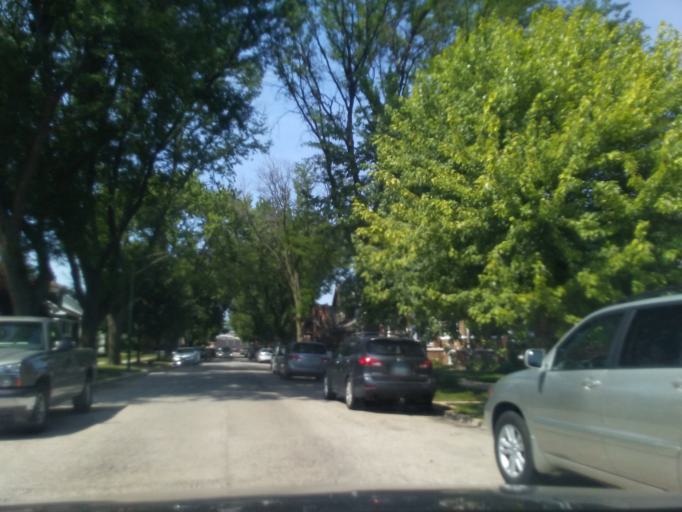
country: US
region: Illinois
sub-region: Cook County
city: Lincolnwood
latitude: 41.9758
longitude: -87.7566
